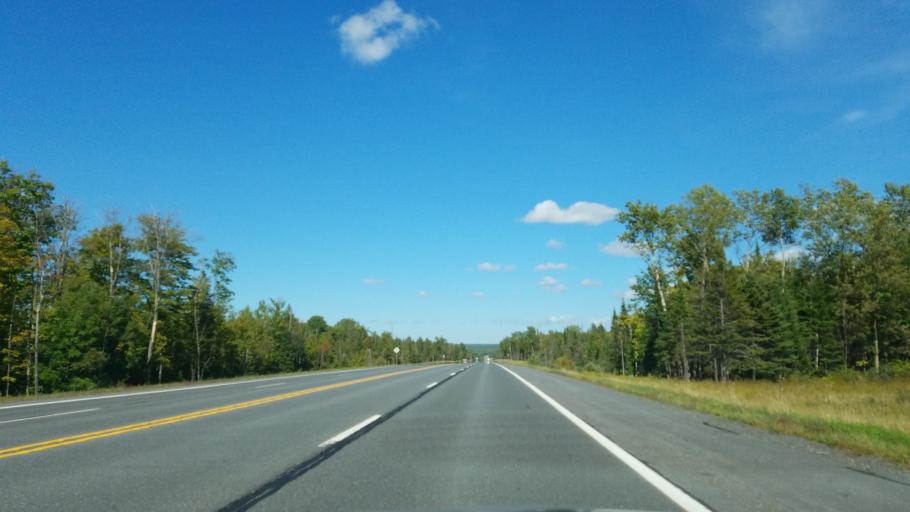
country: US
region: Michigan
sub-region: Baraga County
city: L'Anse
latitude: 46.5568
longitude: -88.5146
